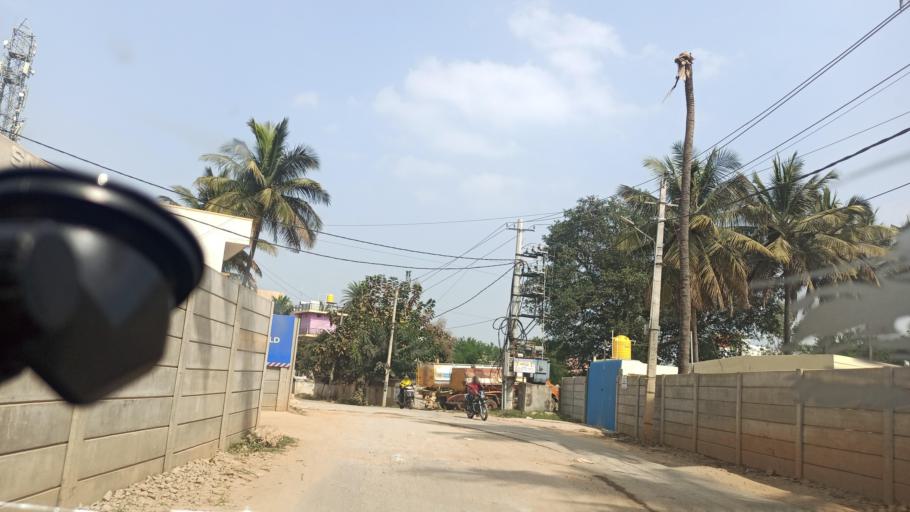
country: IN
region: Karnataka
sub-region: Bangalore Urban
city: Yelahanka
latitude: 13.0856
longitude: 77.6184
